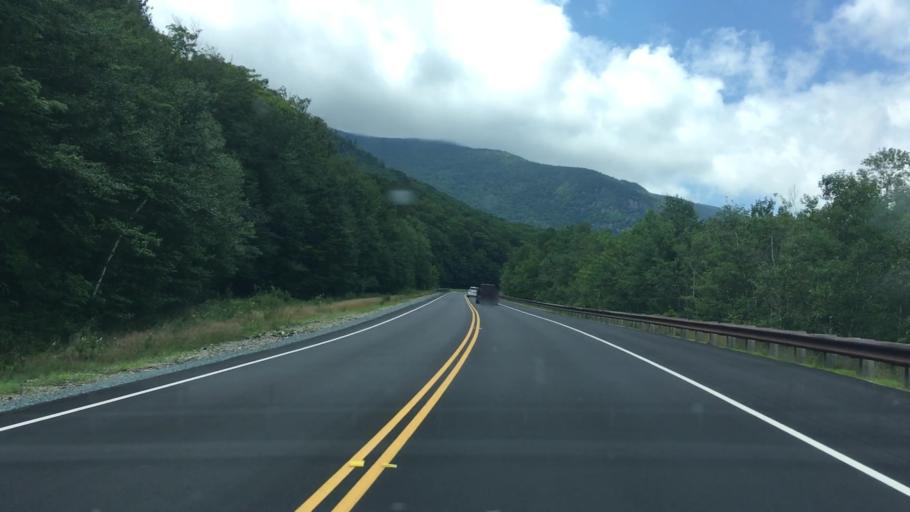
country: US
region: New Hampshire
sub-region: Grafton County
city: Woodstock
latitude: 44.0342
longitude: -71.7727
